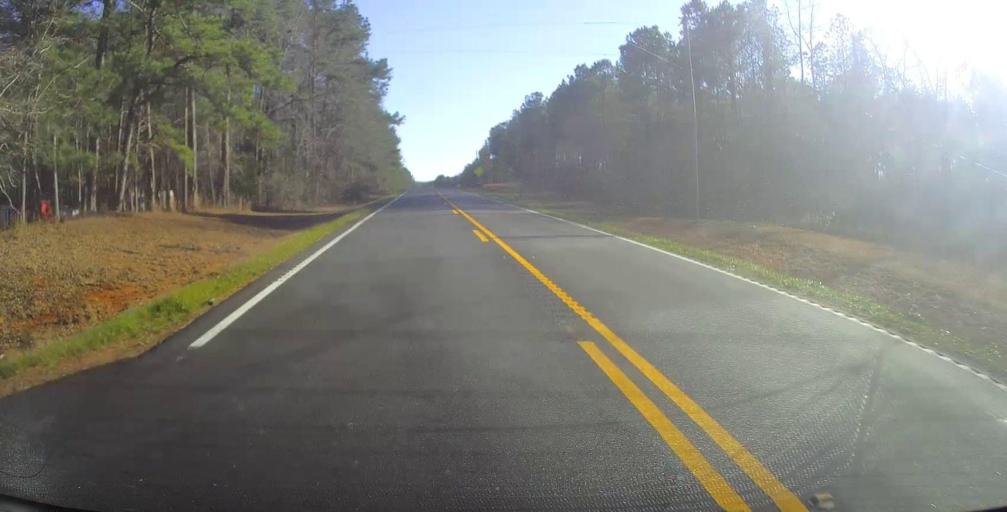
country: US
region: Georgia
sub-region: Talbot County
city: Sardis
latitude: 32.7919
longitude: -84.6928
